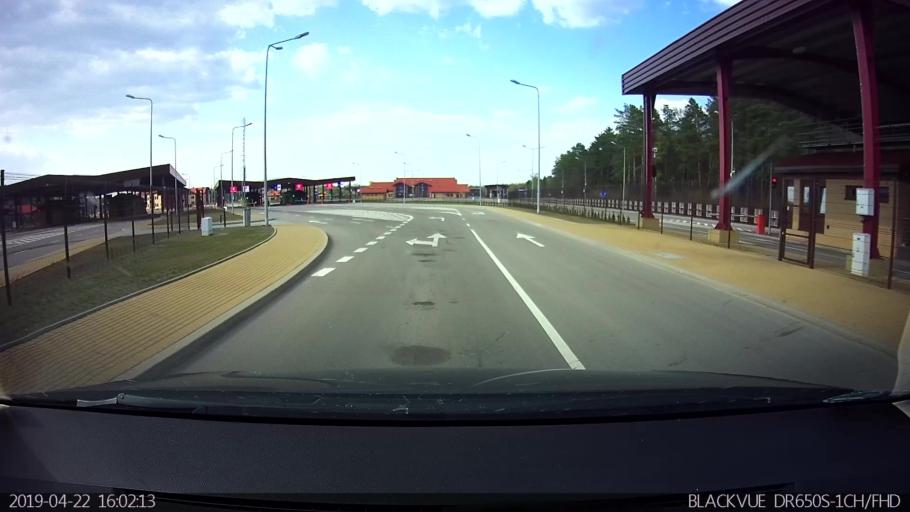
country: PL
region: Podlasie
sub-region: Powiat hajnowski
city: Czeremcha
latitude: 52.4739
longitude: 23.3576
